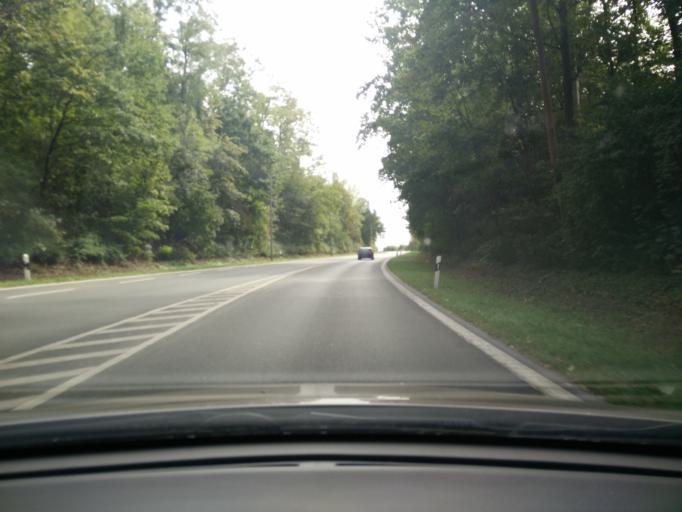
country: DE
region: Bavaria
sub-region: Regierungsbezirk Mittelfranken
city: Seukendorf
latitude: 49.4863
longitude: 10.9315
